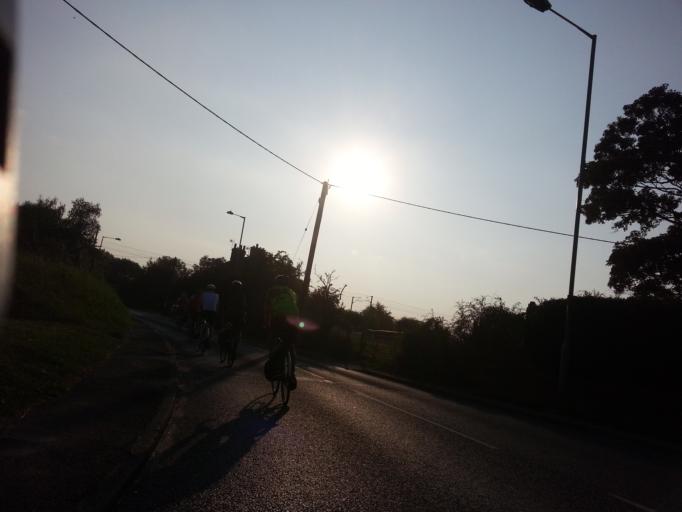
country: GB
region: England
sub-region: Suffolk
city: Bramford
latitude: 52.0764
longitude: 1.1065
